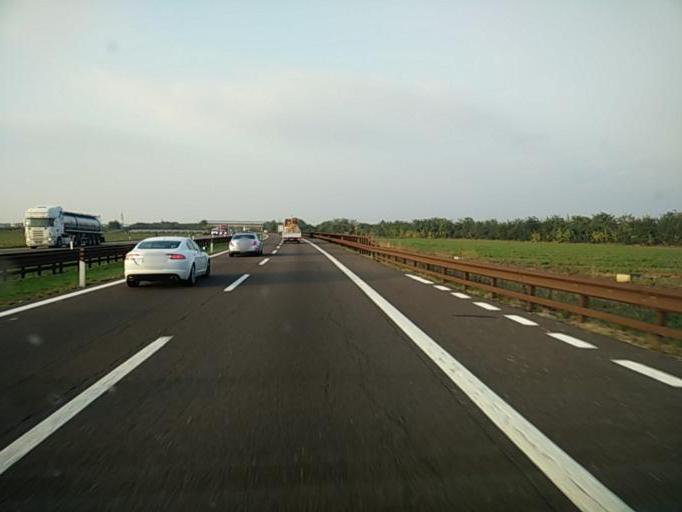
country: IT
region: Veneto
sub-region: Provincia di Verona
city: Alpo
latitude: 45.3608
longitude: 10.9207
